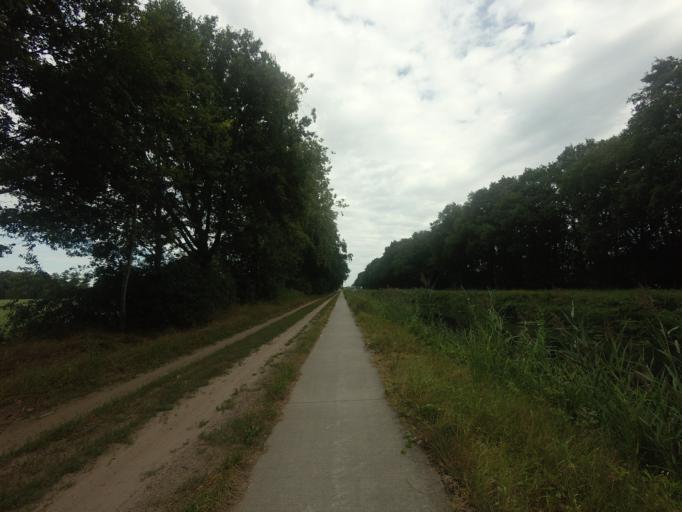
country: NL
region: Overijssel
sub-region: Gemeente Raalte
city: Raalte
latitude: 52.4382
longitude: 6.3313
